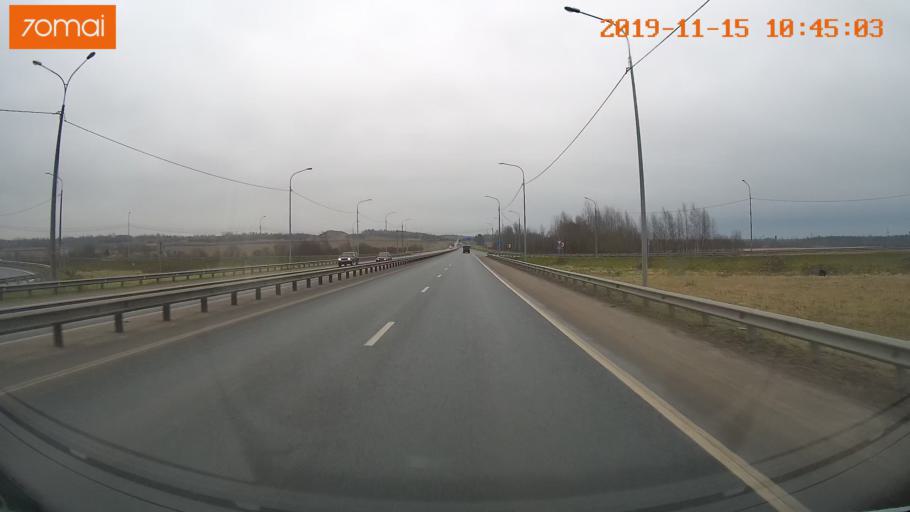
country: RU
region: Vologda
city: Sheksna
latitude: 59.2113
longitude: 38.5760
